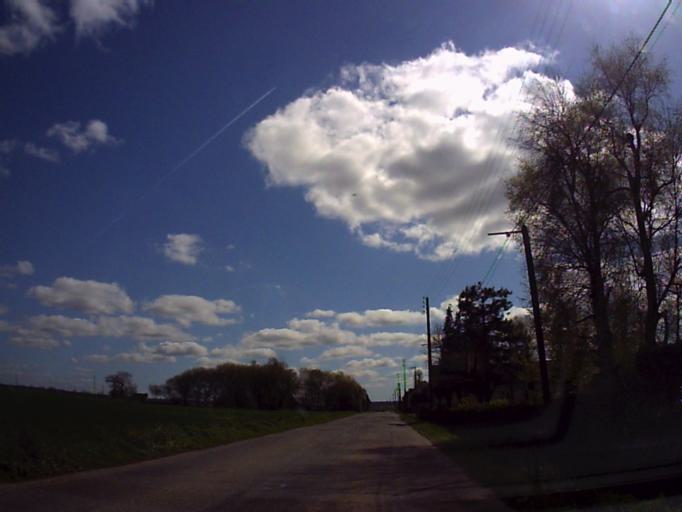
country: FR
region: Brittany
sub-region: Departement d'Ille-et-Vilaine
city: Saint-Meen-le-Grand
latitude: 48.1444
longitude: -2.1558
